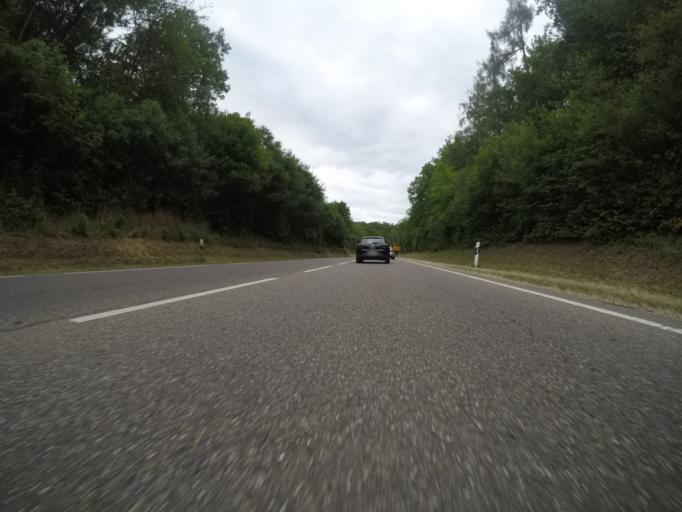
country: DE
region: Baden-Wuerttemberg
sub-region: Regierungsbezirk Stuttgart
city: Korntal
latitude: 48.8098
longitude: 9.1287
